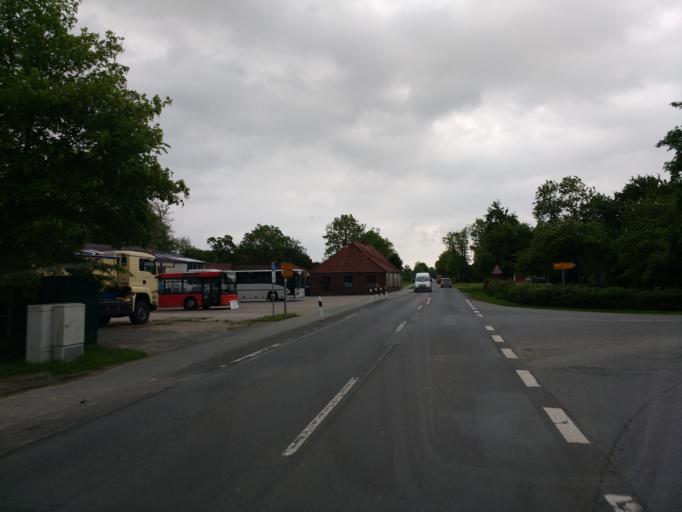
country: DE
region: Lower Saxony
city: Schillig
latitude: 53.6375
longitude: 8.0090
